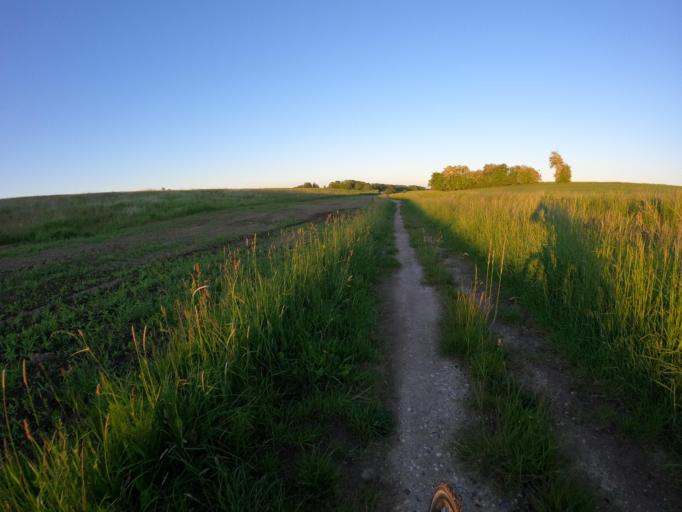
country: DK
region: Zealand
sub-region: Greve Kommune
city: Tune
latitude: 55.6258
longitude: 12.2358
